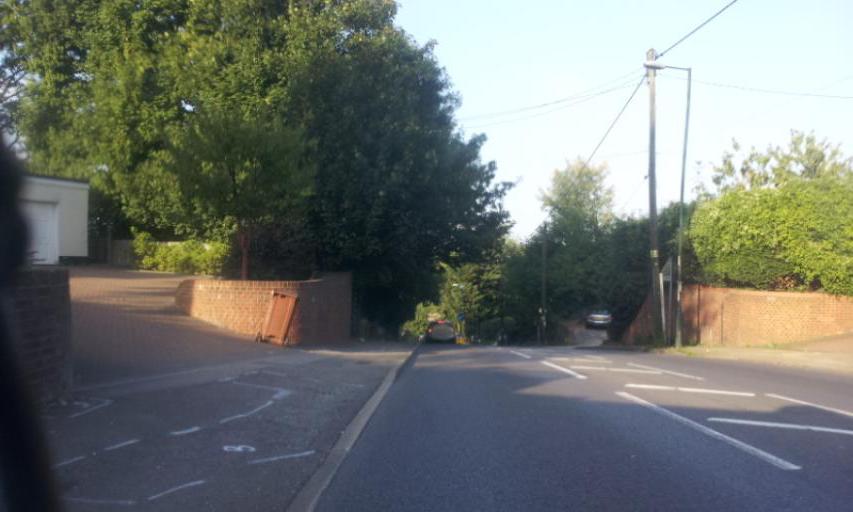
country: GB
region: England
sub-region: Kent
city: Boxley
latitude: 51.3364
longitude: 0.5222
